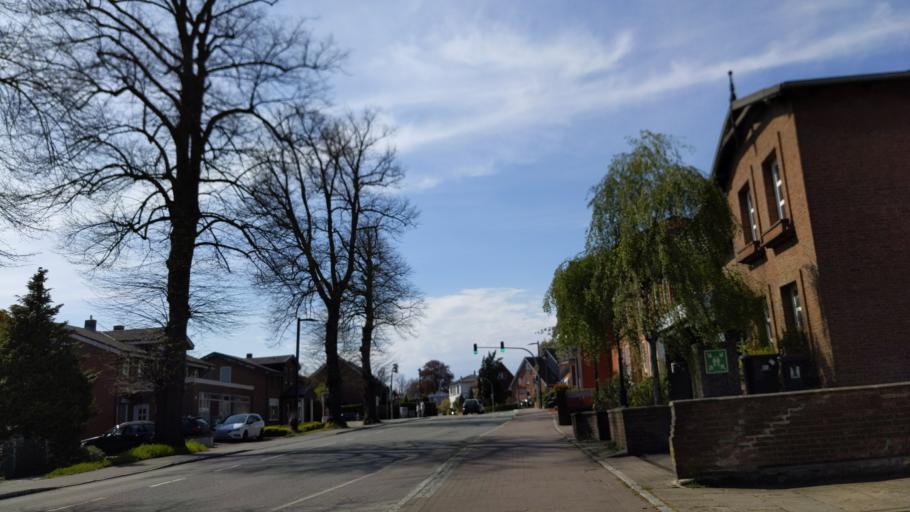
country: DE
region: Schleswig-Holstein
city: Bad Schwartau
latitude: 53.9207
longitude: 10.6857
